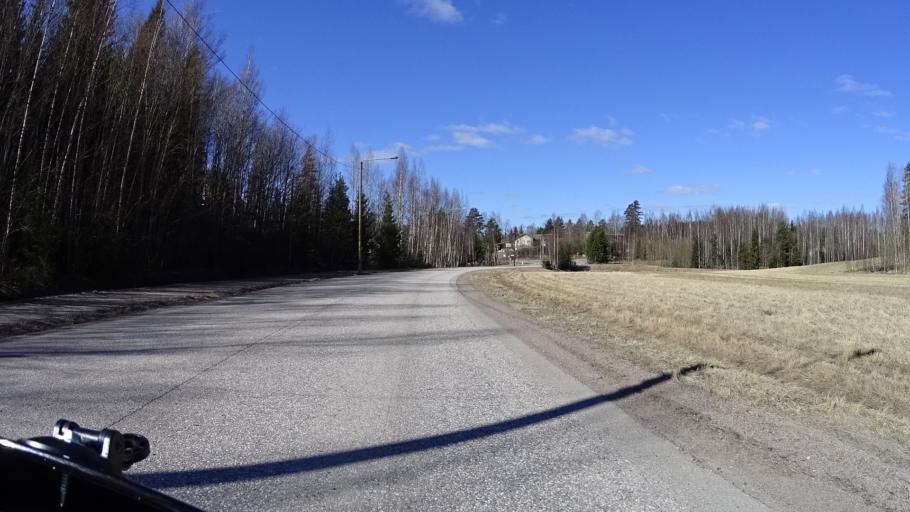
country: FI
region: Uusimaa
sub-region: Helsinki
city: Kauniainen
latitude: 60.3220
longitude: 24.7222
